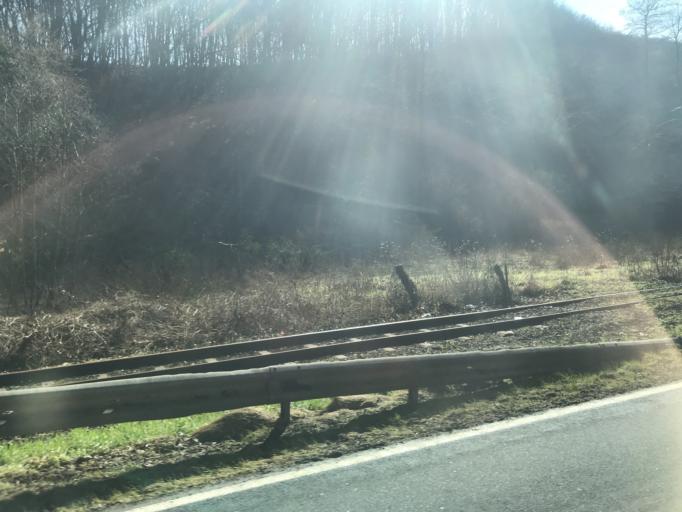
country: DE
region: Rheinland-Pfalz
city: Brohl-Lutzing
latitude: 50.4717
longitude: 7.3102
